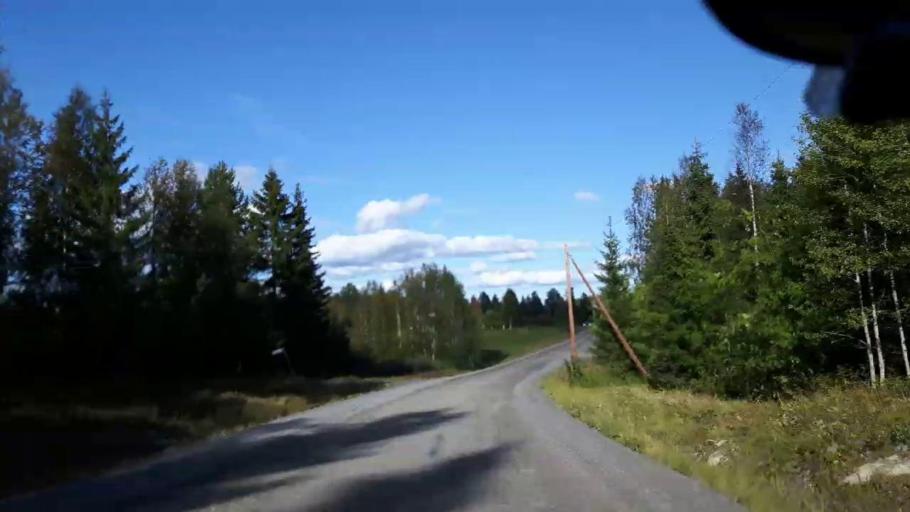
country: SE
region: Jaemtland
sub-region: Ragunda Kommun
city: Hammarstrand
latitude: 63.4328
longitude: 16.1814
